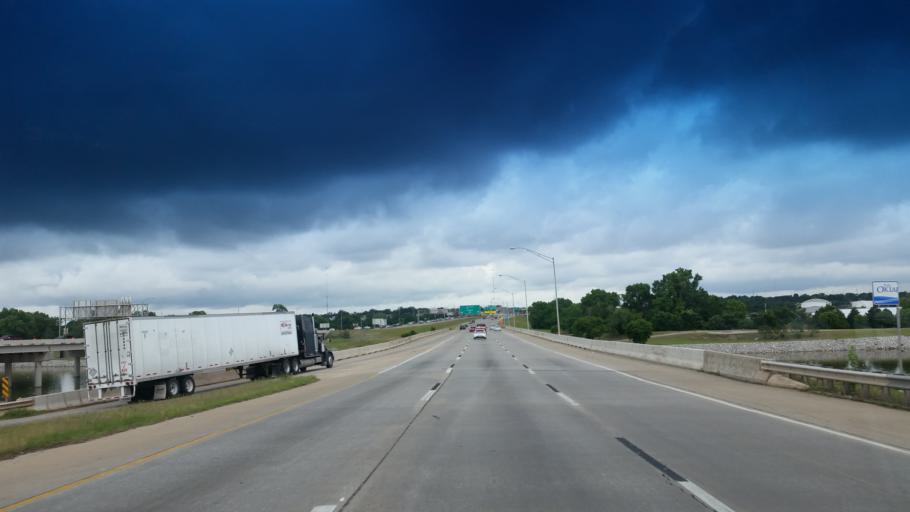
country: US
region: Oklahoma
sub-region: Oklahoma County
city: Oklahoma City
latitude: 35.4601
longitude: -97.4933
